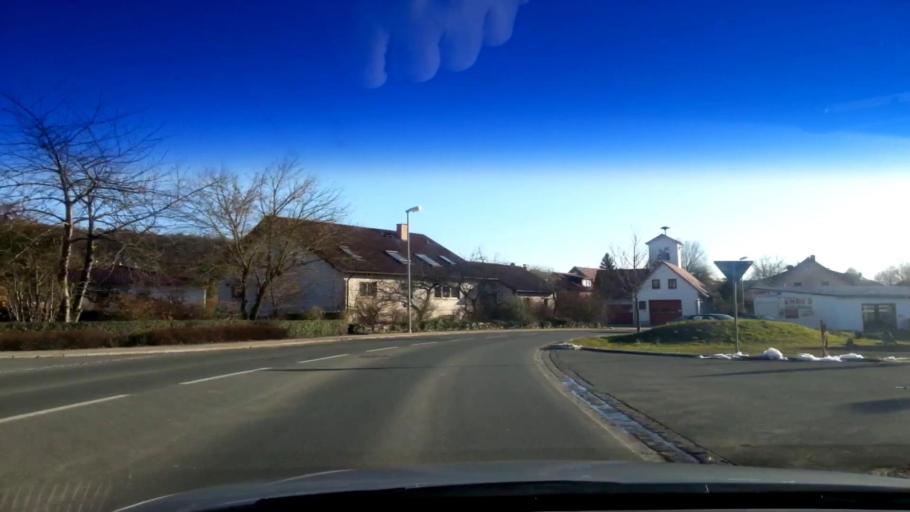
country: DE
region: Bavaria
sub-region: Upper Franconia
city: Litzendorf
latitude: 49.9272
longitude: 11.0070
